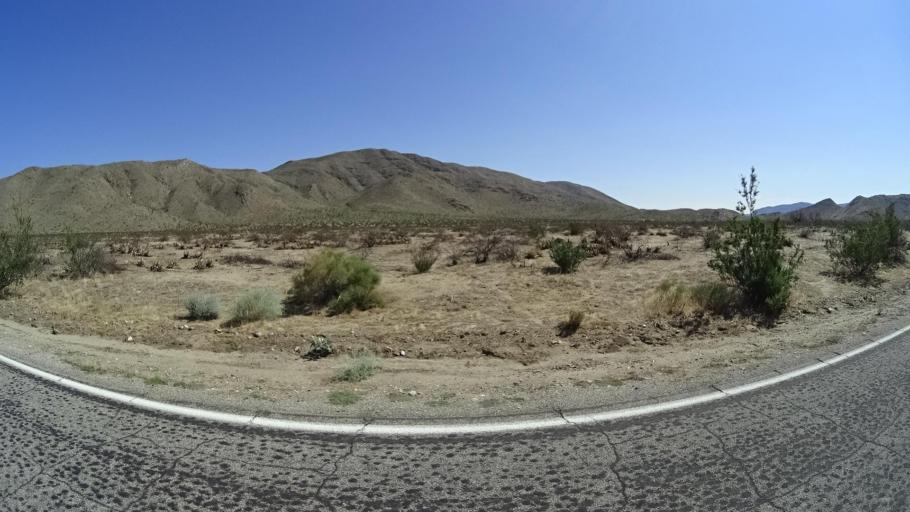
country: US
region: California
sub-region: San Diego County
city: Julian
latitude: 32.9877
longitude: -116.4435
